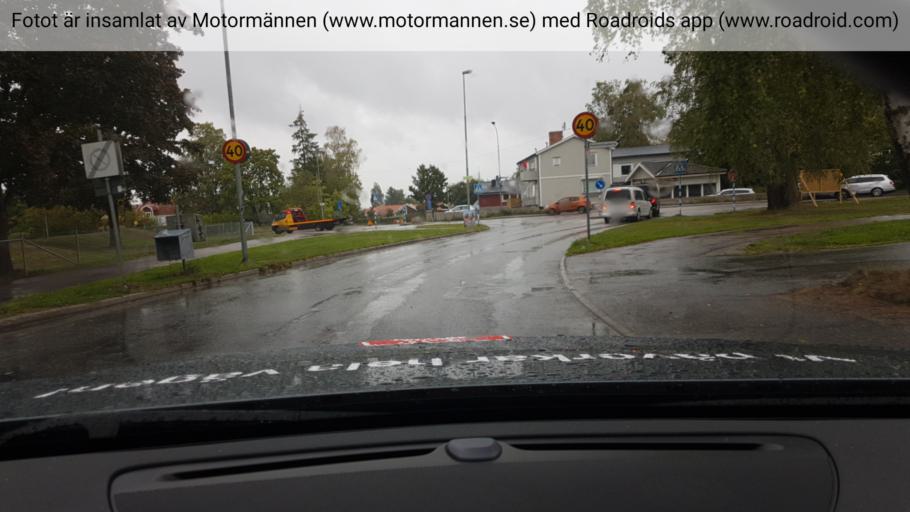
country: SE
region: Stockholm
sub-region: Haninge Kommun
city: Haninge
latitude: 59.1716
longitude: 18.1485
